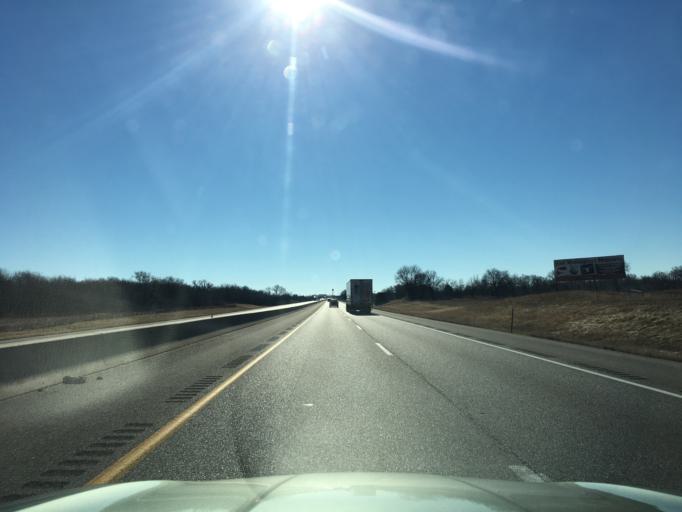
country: US
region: Kansas
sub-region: Sumner County
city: Belle Plaine
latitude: 37.3880
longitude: -97.3251
